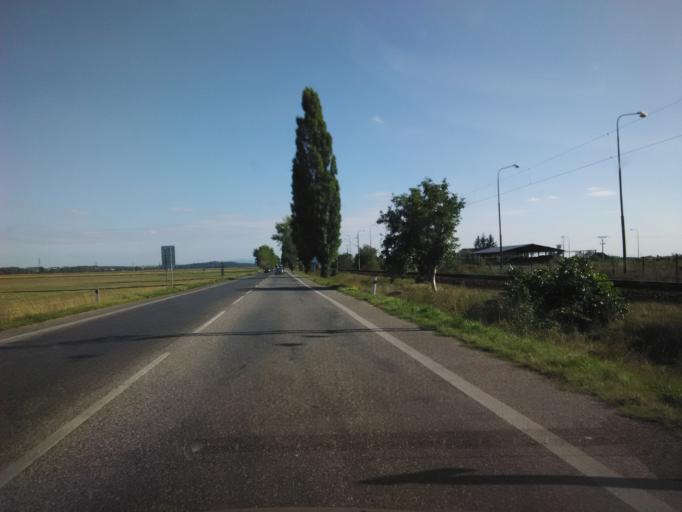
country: SK
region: Nitriansky
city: Tlmace
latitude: 48.2773
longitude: 18.5529
